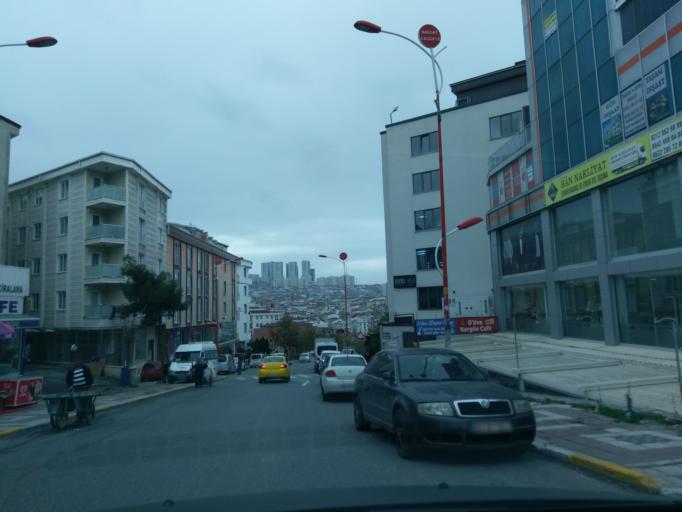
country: TR
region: Istanbul
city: Esenyurt
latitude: 41.0184
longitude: 28.6656
